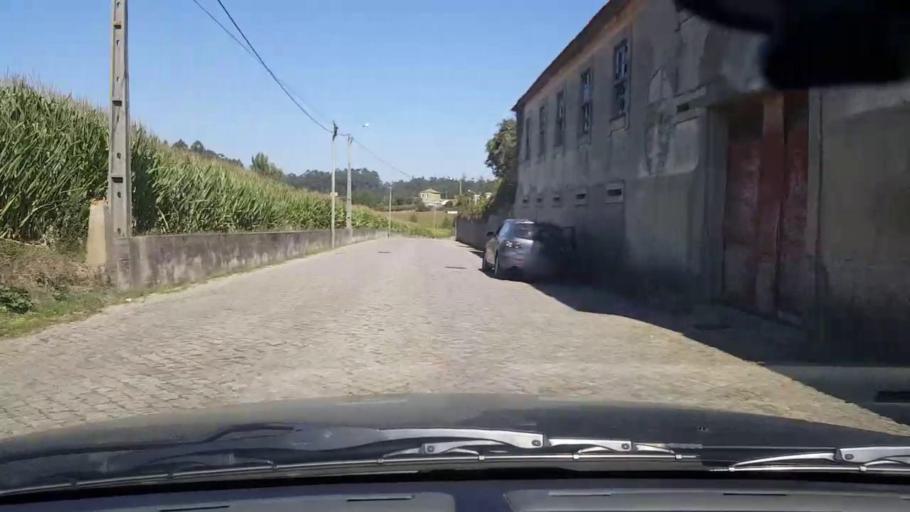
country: PT
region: Porto
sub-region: Matosinhos
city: Lavra
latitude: 41.2694
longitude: -8.6951
